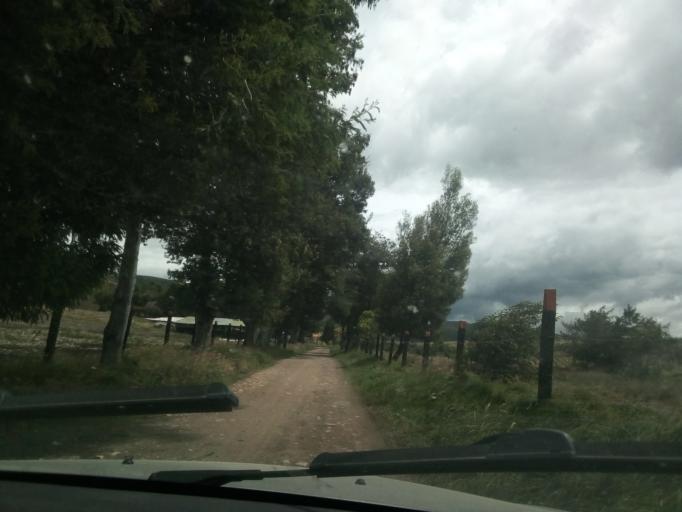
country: CO
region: Boyaca
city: Toca
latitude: 5.6095
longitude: -73.1116
